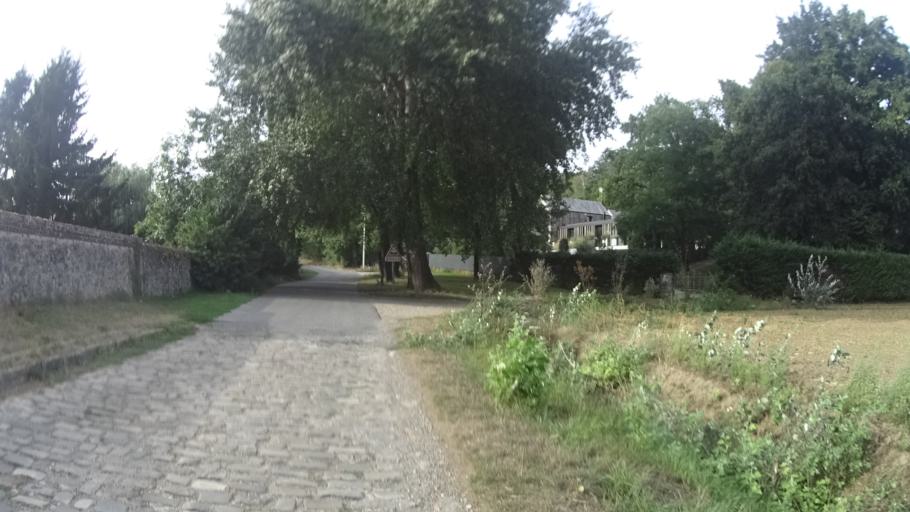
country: FR
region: Picardie
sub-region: Departement de l'Oise
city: Ver-sur-Launette
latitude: 49.1284
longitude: 2.7026
